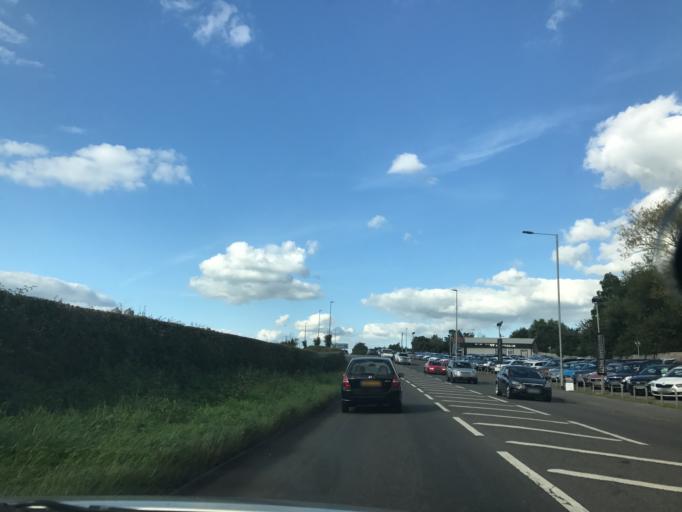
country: GB
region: England
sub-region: Cheshire East
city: Willaston
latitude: 53.0931
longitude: -2.4873
